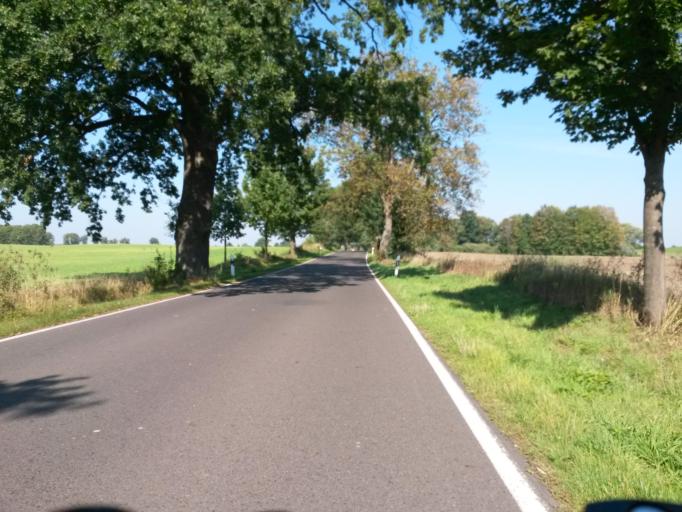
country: DE
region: Brandenburg
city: Templin
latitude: 53.0641
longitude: 13.4348
